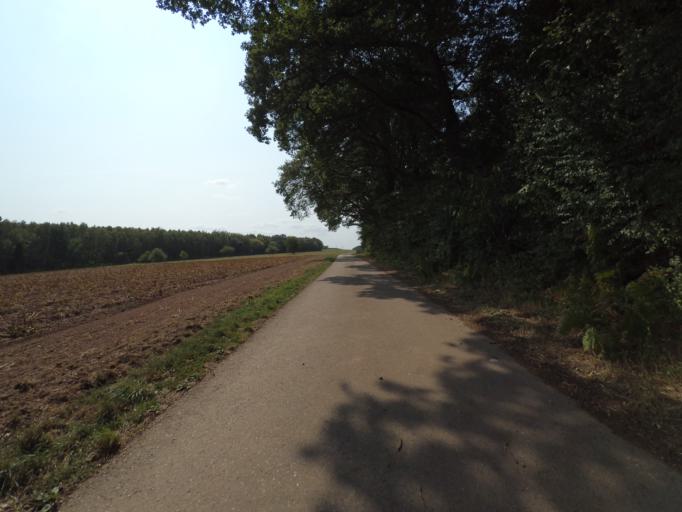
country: DE
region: Rheinland-Pfalz
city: Taben-Rodt
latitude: 49.5352
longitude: 6.5720
